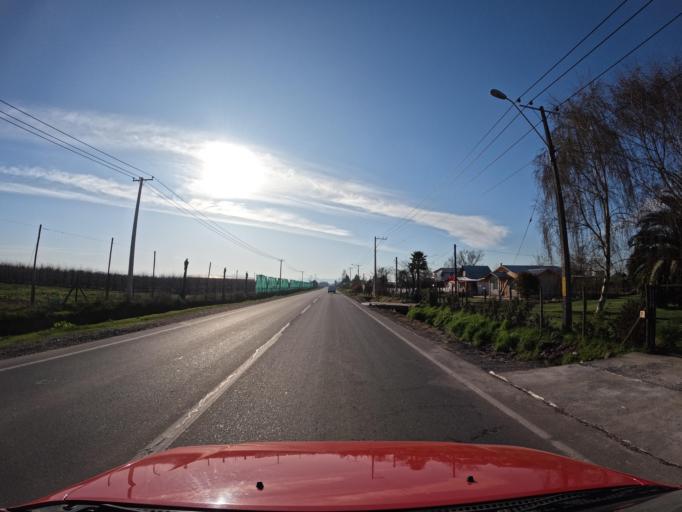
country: CL
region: Maule
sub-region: Provincia de Curico
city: Teno
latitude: -34.8974
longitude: -71.0601
